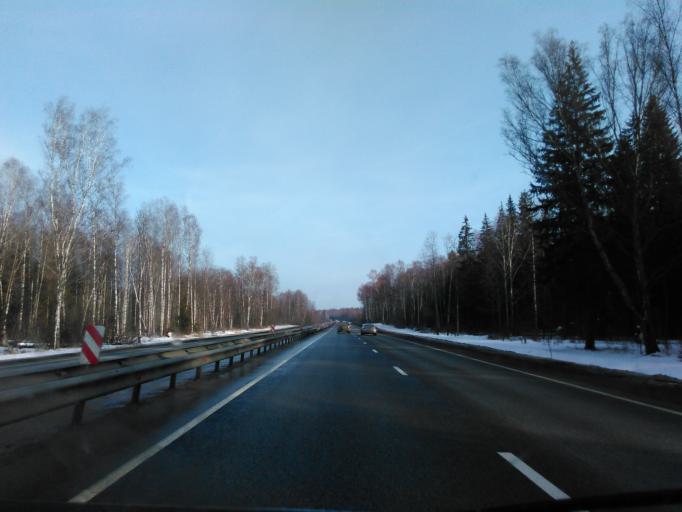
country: RU
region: Smolensk
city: Vyaz'ma
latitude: 55.1935
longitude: 33.9416
